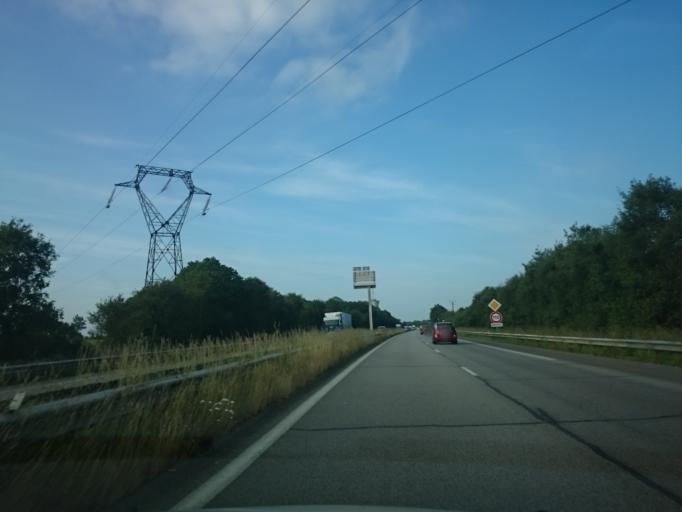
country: FR
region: Brittany
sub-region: Departement du Finistere
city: Landrevarzec
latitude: 48.0946
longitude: -4.0339
